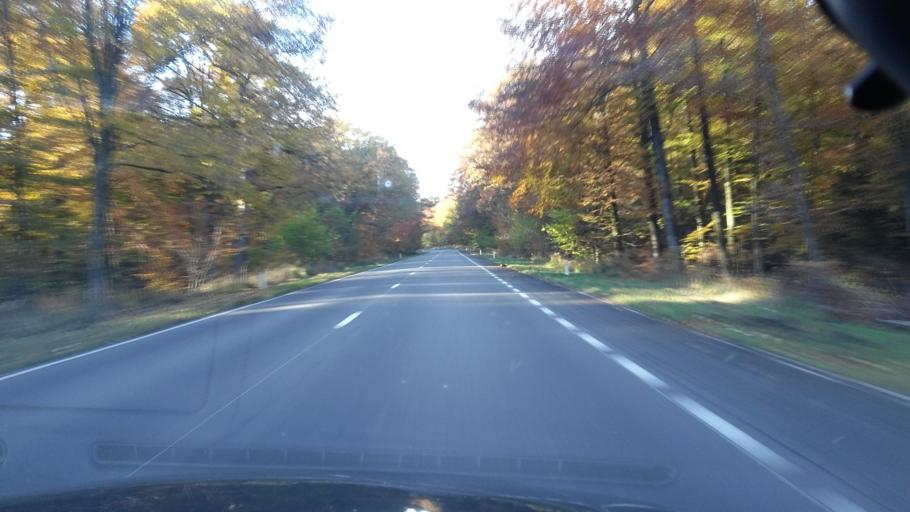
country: BE
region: Wallonia
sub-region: Province du Luxembourg
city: Herbeumont
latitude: 49.7532
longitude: 5.2055
